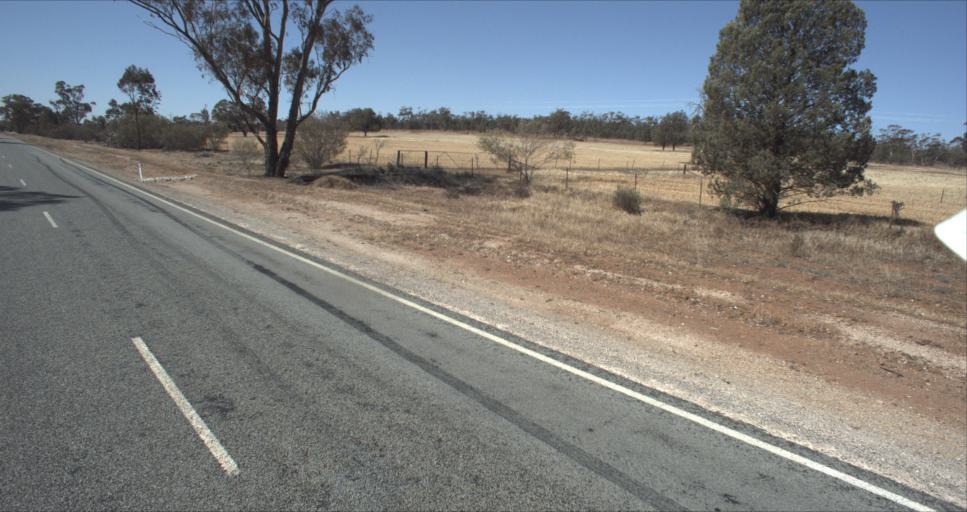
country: AU
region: New South Wales
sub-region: Leeton
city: Leeton
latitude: -34.4793
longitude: 146.4345
